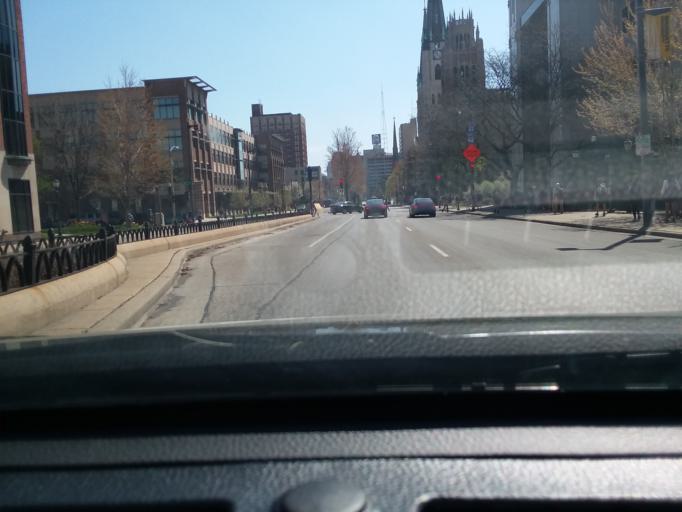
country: US
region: Wisconsin
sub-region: Milwaukee County
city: Milwaukee
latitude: 43.0386
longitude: -87.9296
